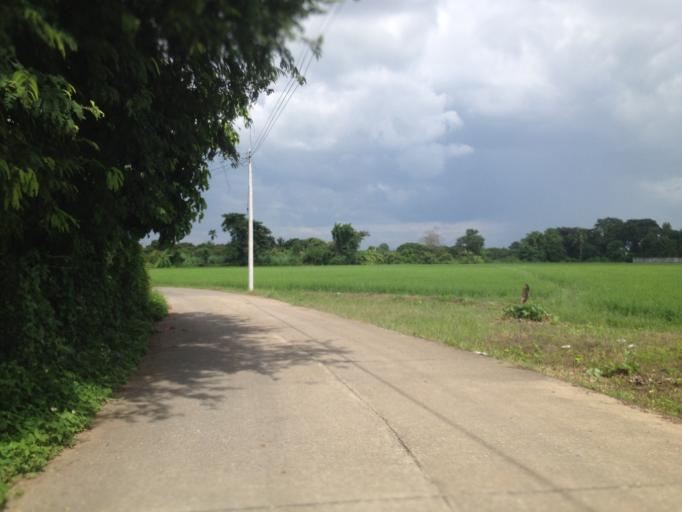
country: TH
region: Chiang Mai
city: Hang Dong
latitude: 18.6885
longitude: 98.9061
